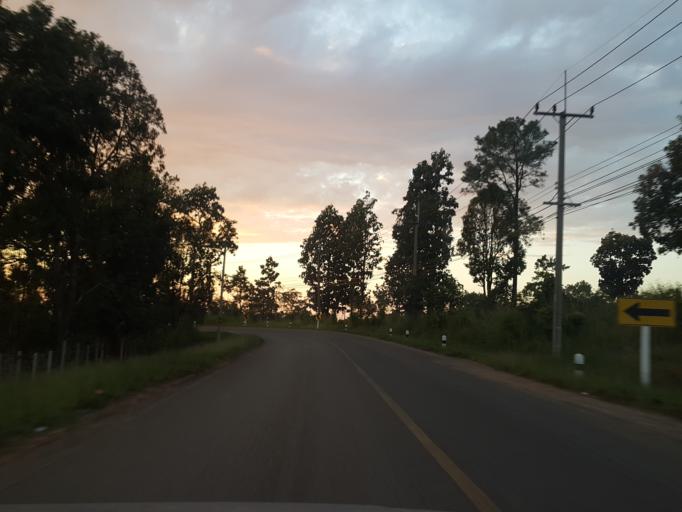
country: TH
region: Mae Hong Son
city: Khun Yuam
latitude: 18.8458
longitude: 97.9611
